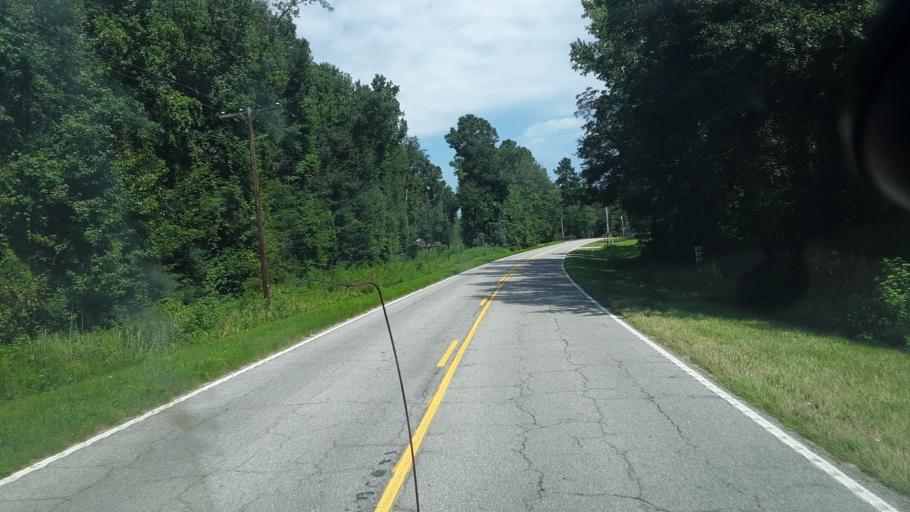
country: US
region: South Carolina
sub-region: Bamberg County
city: Bamberg
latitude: 33.2738
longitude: -81.0434
